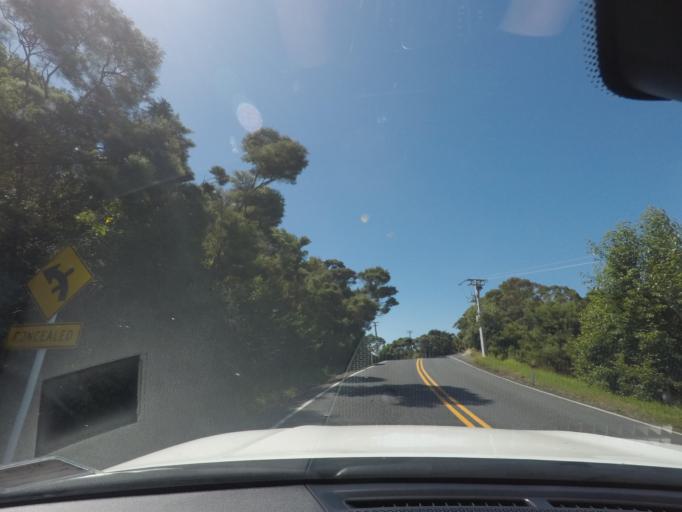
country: NZ
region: Auckland
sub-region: Auckland
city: Parakai
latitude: -36.5788
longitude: 174.3261
